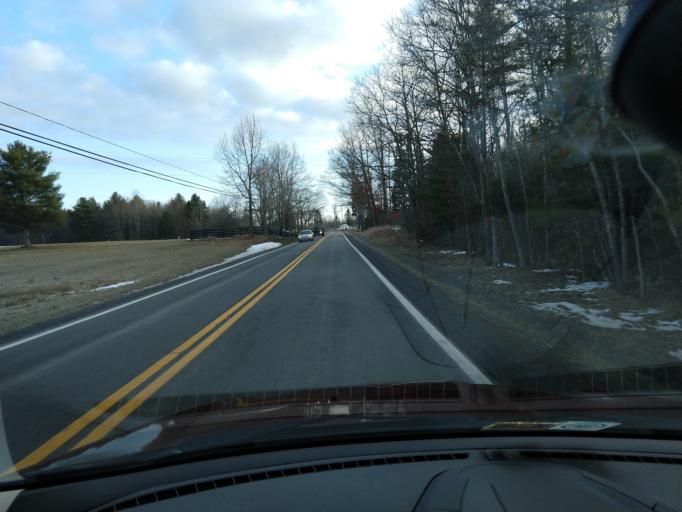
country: US
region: West Virginia
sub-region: Pocahontas County
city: Marlinton
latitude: 38.0750
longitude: -80.2864
